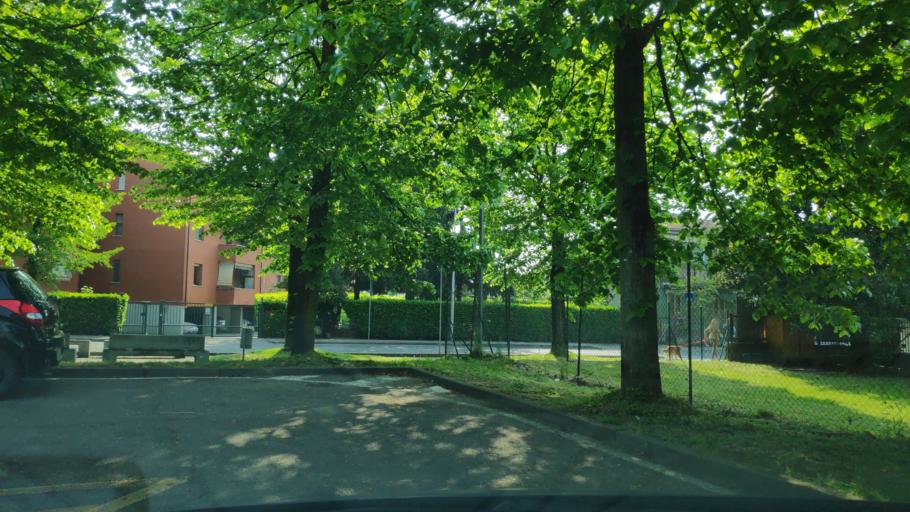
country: IT
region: Lombardy
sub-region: Citta metropolitana di Milano
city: Vizzolo Predabissi
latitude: 45.3575
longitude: 9.3469
